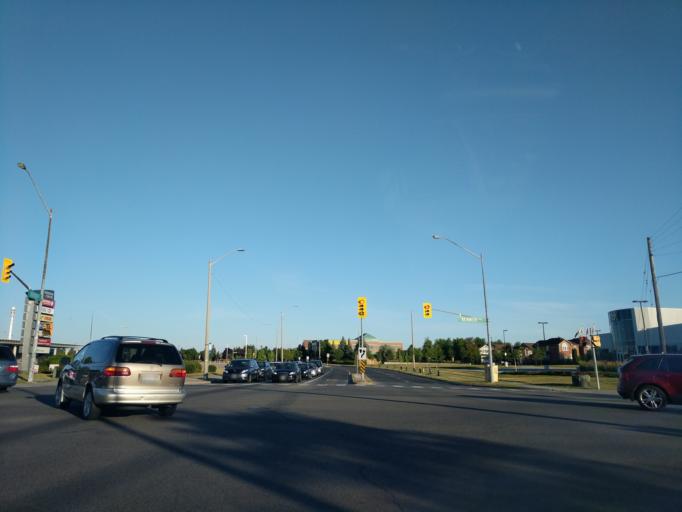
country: CA
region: Ontario
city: Markham
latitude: 43.8345
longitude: -79.3040
